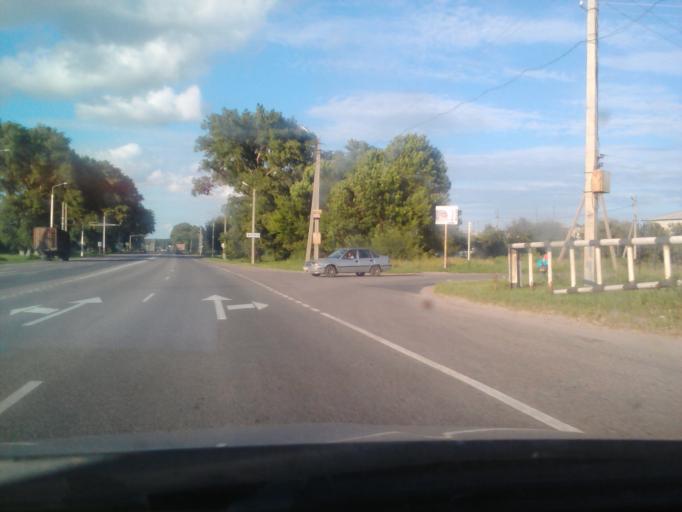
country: RU
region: Kursk
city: Kurchatov
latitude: 51.6610
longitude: 35.7203
